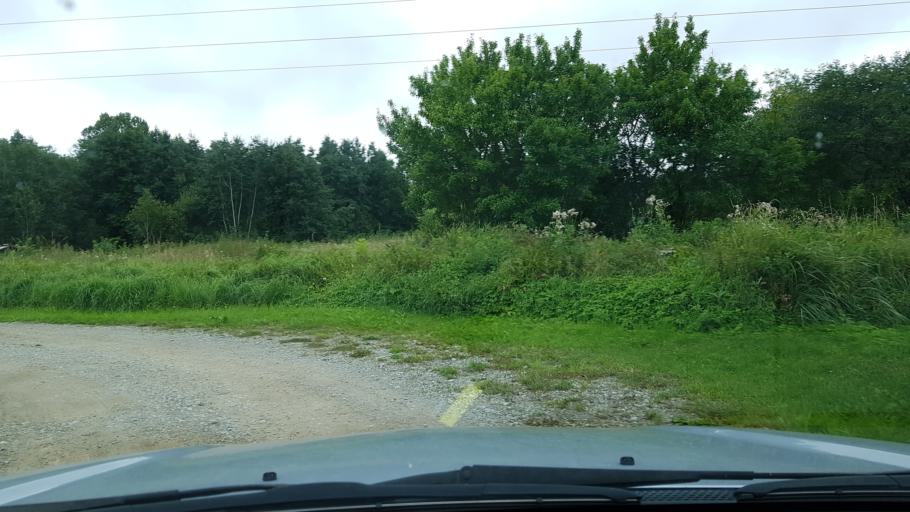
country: EE
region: Harju
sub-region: Rae vald
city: Jueri
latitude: 59.3539
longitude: 24.9216
